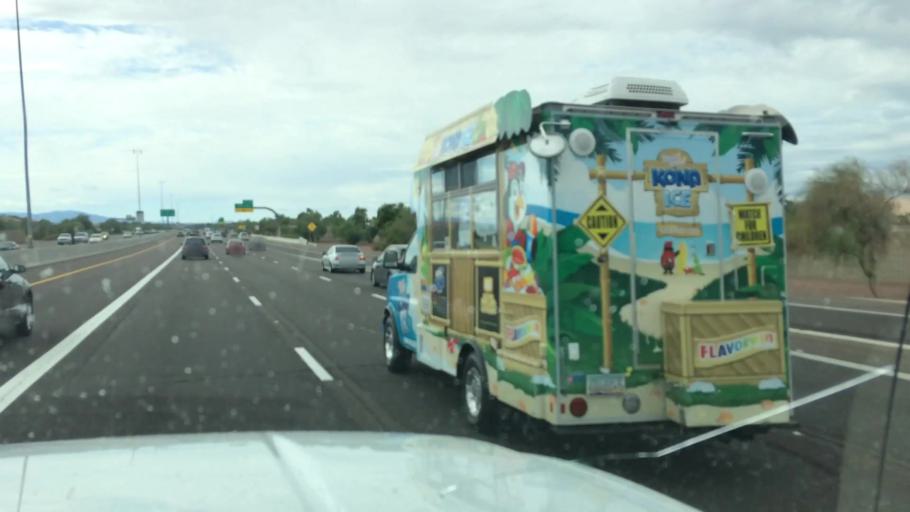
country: US
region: Arizona
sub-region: Maricopa County
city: Peoria
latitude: 33.6679
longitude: -112.1762
